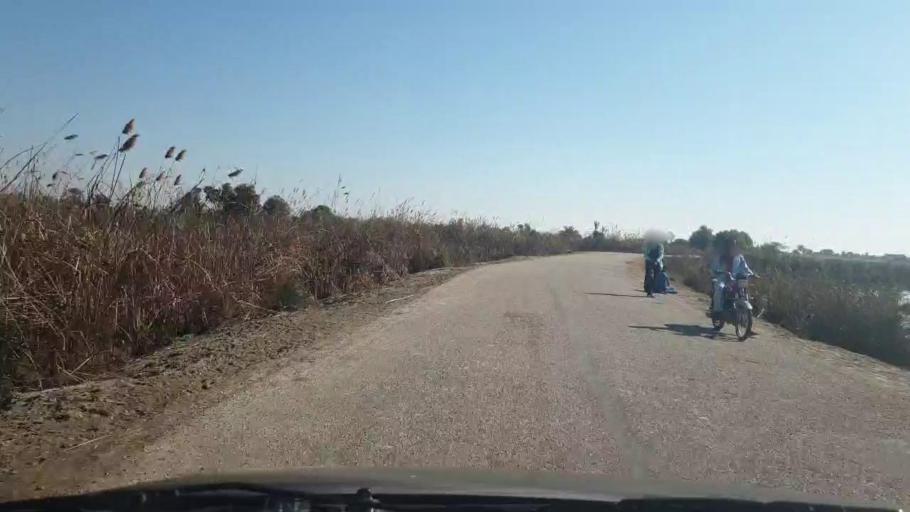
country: PK
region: Sindh
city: Bozdar
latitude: 27.1594
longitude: 68.6473
